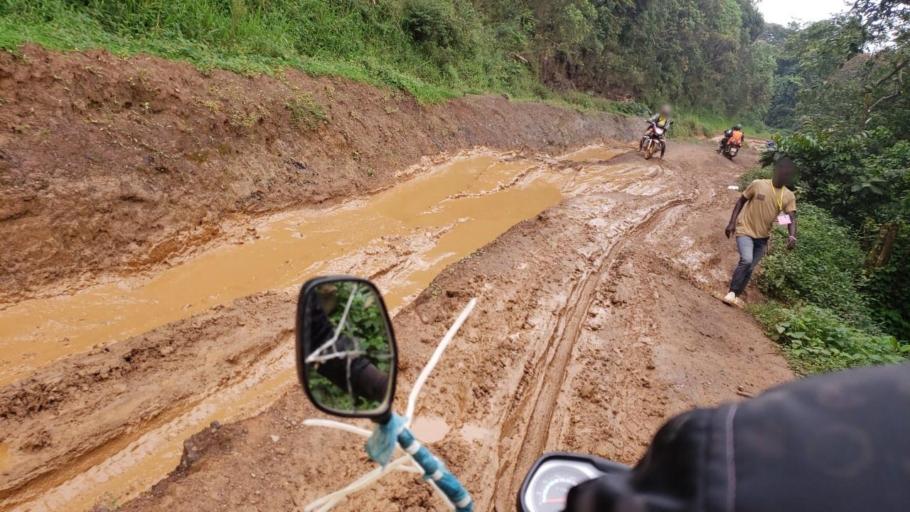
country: CD
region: South Kivu
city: Kabare
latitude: -2.2537
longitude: 28.6468
